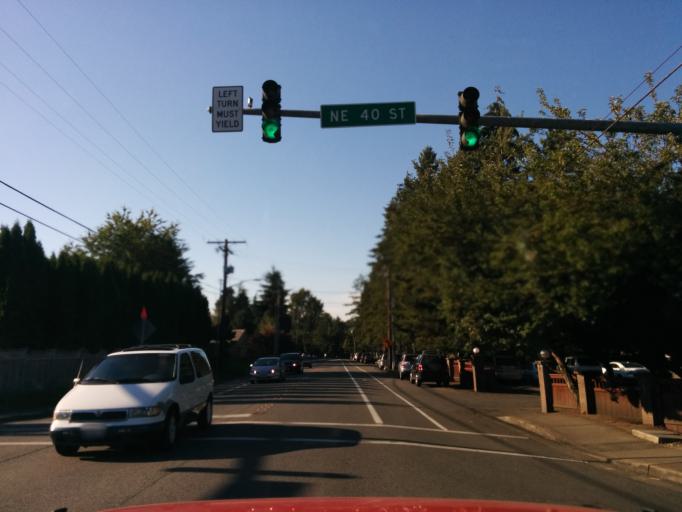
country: US
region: Washington
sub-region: King County
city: Sammamish
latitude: 47.6461
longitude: -122.1079
